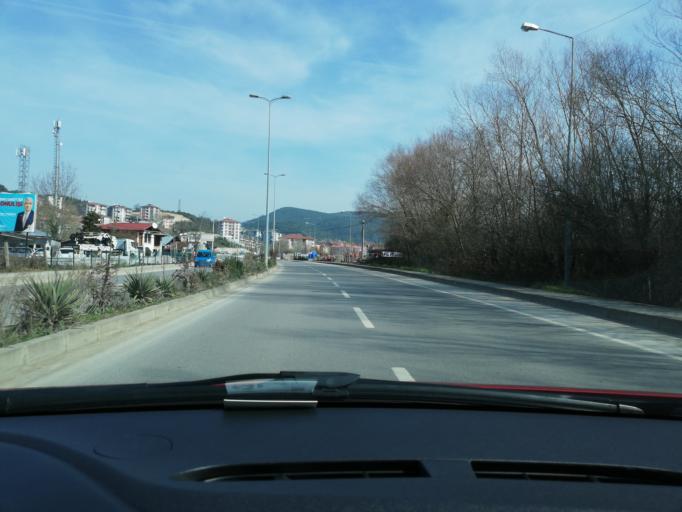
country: TR
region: Bartin
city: Bartin
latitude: 41.6393
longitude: 32.3540
